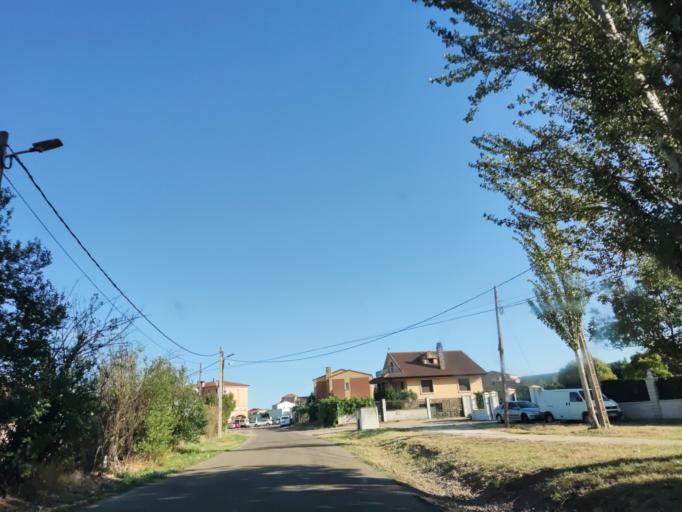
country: ES
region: Castille and Leon
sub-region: Provincia de Zamora
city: Villaralbo
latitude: 41.4957
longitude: -5.6843
